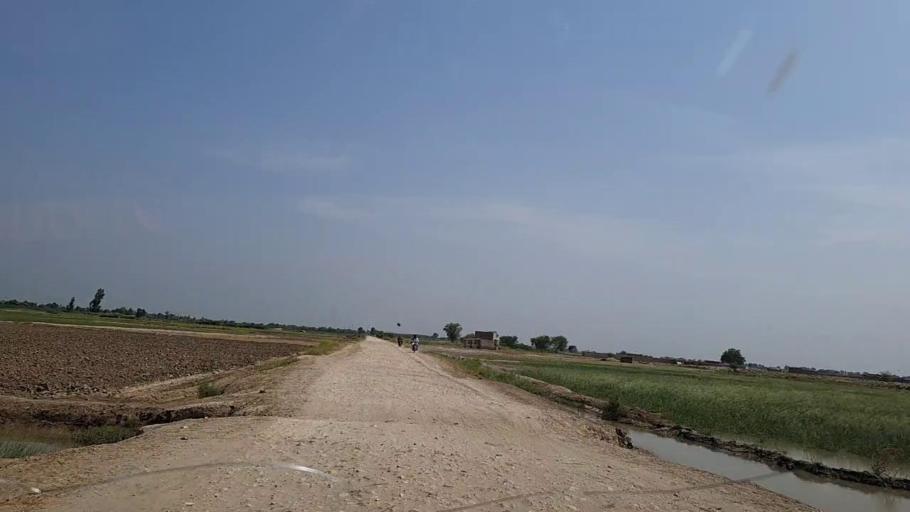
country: PK
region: Sindh
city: Khanpur
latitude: 27.8000
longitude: 69.3133
